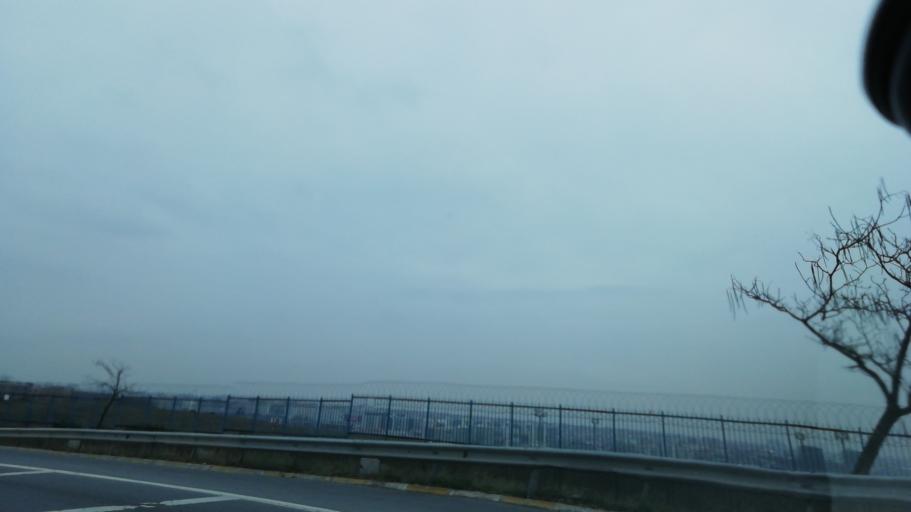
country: TR
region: Istanbul
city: Bahcelievler
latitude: 40.9976
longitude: 28.7992
